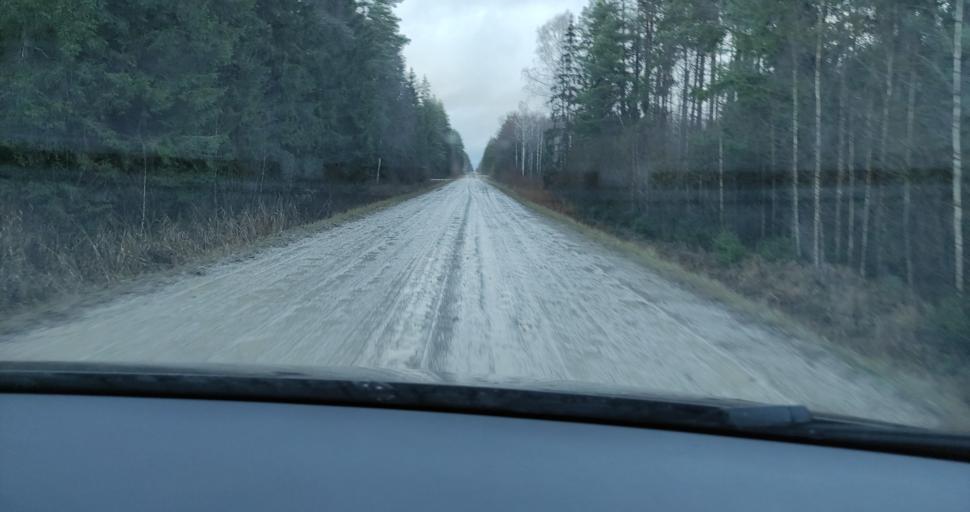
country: LV
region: Skrunda
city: Skrunda
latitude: 56.7300
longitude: 22.2036
